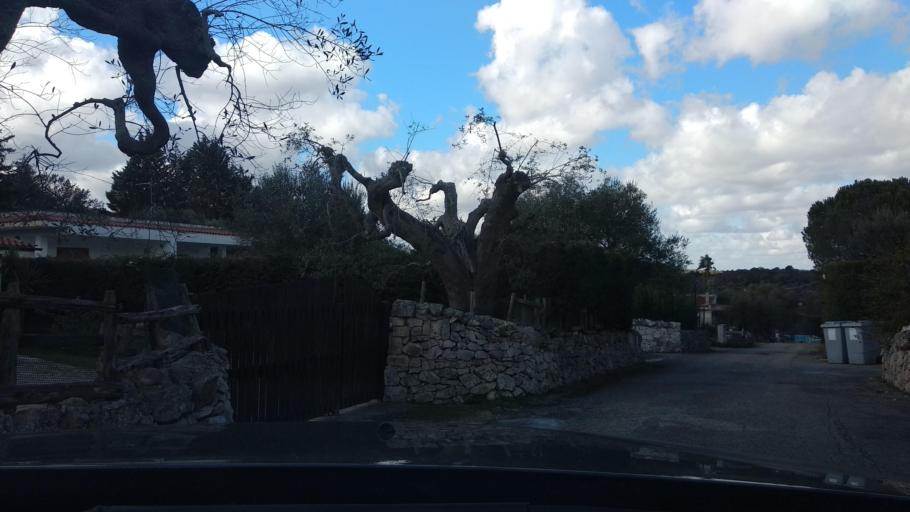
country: IT
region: Apulia
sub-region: Provincia di Brindisi
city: Casalini
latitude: 40.6899
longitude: 17.4855
